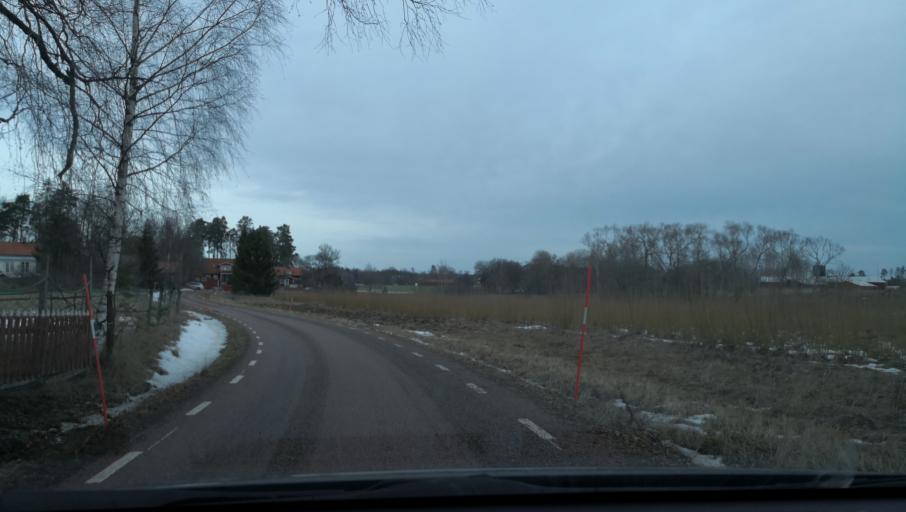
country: SE
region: Vaestmanland
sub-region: Vasteras
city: Skultuna
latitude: 59.6151
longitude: 16.4094
